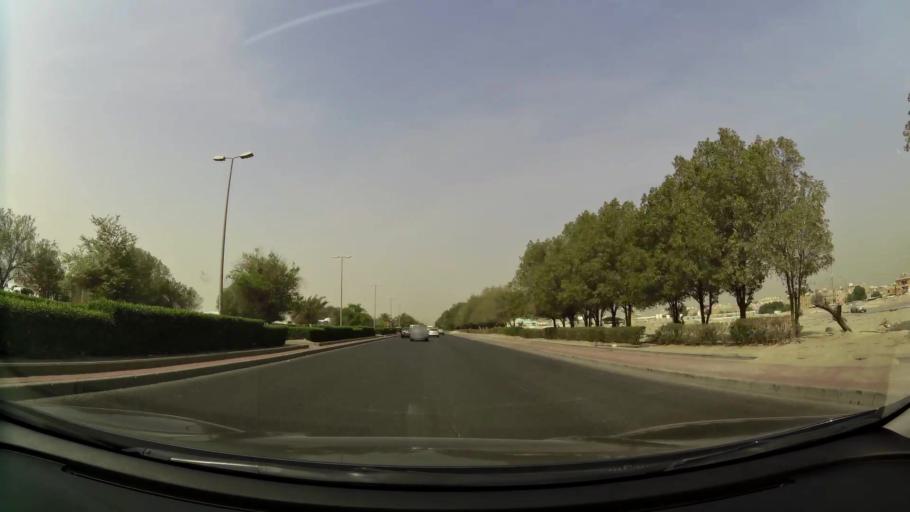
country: KW
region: Al Asimah
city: Ar Rabiyah
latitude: 29.2560
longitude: 47.9187
